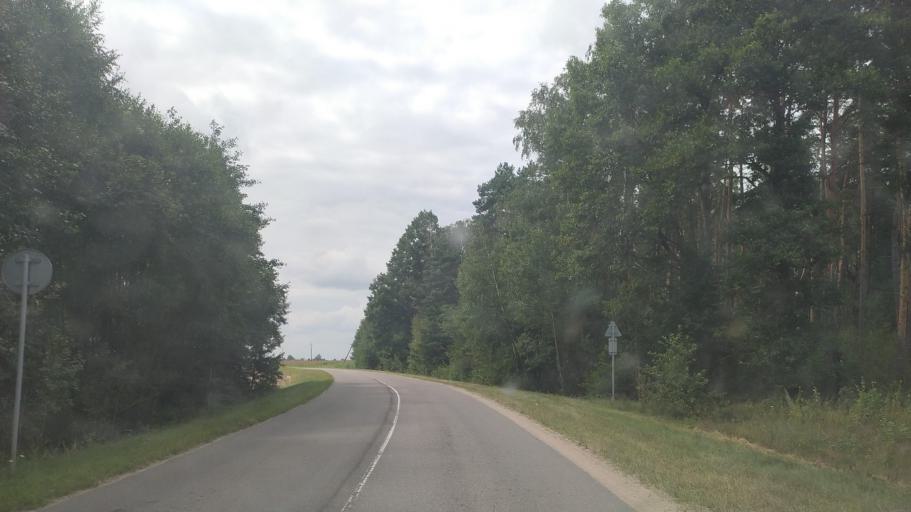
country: BY
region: Brest
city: Byelaazyorsk
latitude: 52.5423
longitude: 25.1345
